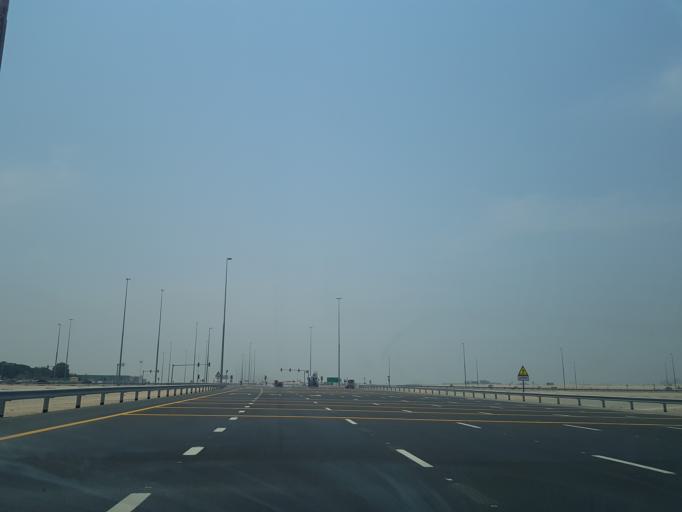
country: AE
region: Dubai
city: Dubai
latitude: 25.0254
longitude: 55.2415
